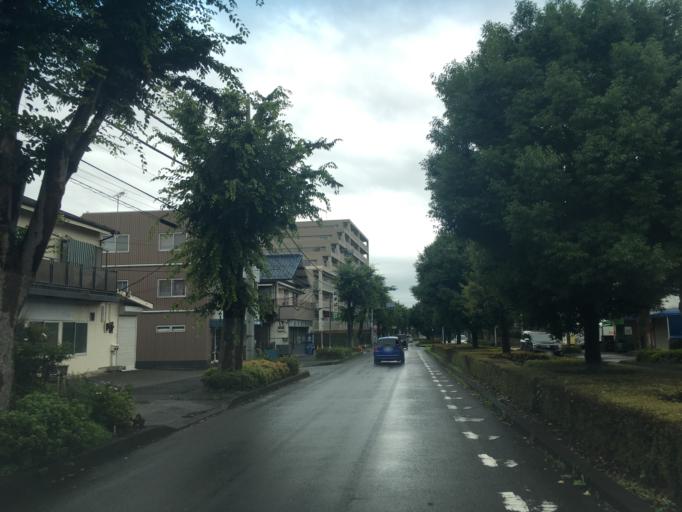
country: JP
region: Tokyo
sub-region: Machida-shi
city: Machida
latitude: 35.5773
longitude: 139.4216
